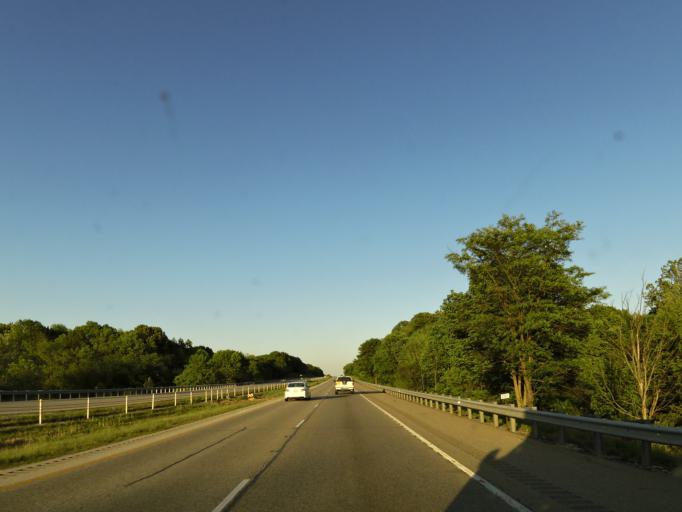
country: US
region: Illinois
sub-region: Vermilion County
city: Danville
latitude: 40.1149
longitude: -87.5839
